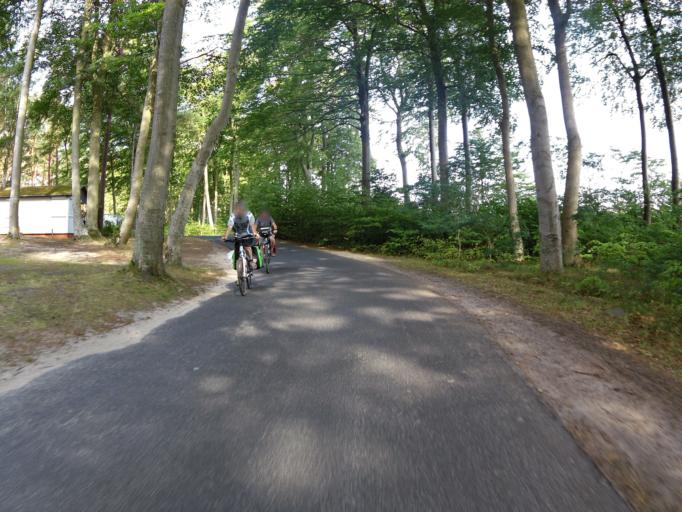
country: DE
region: Mecklenburg-Vorpommern
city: Seebad Bansin
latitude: 54.0034
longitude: 14.0934
